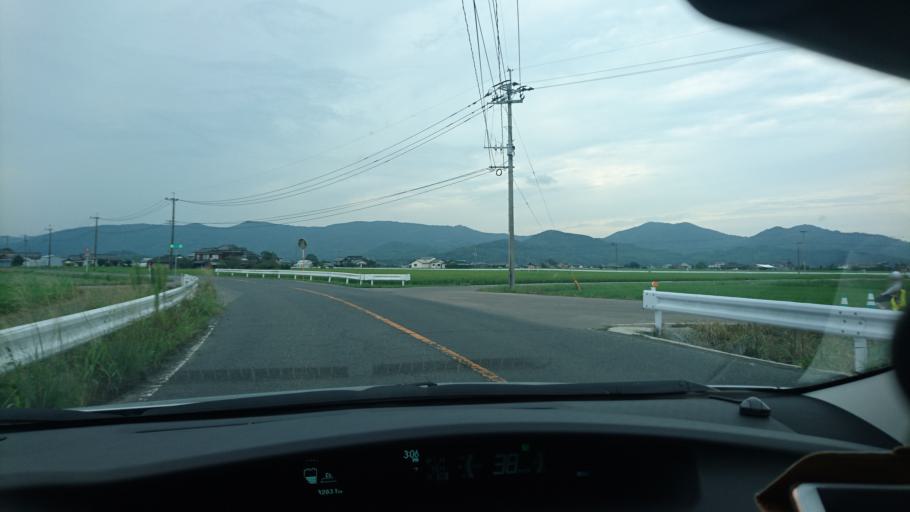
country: JP
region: Saga Prefecture
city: Takeocho-takeo
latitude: 33.1991
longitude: 130.1156
